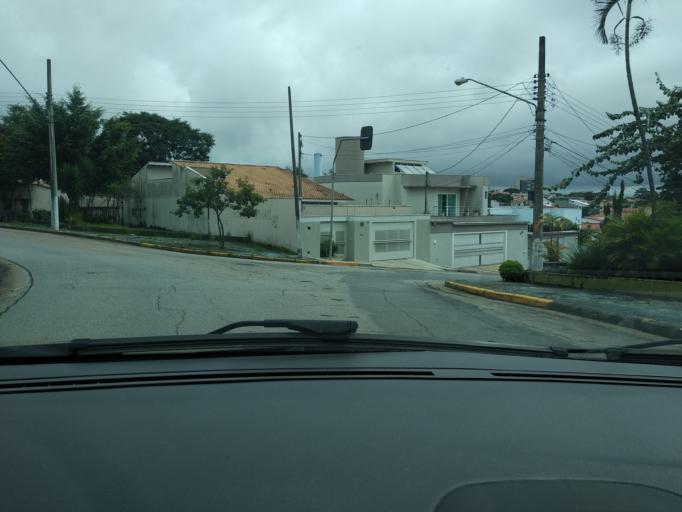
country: BR
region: Sao Paulo
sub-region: Mogi das Cruzes
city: Mogi das Cruzes
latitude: -23.5263
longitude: -46.1770
